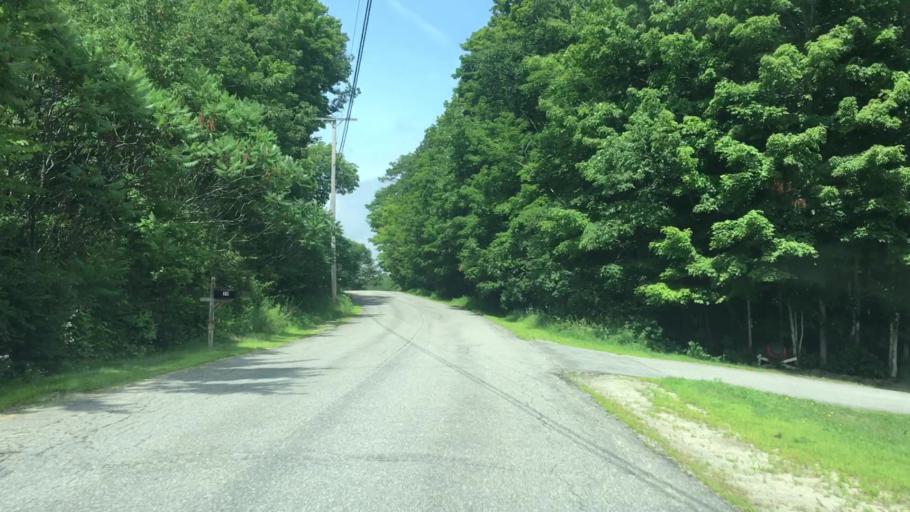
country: US
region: Maine
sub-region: Cumberland County
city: Brunswick
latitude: 43.8884
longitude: -69.9082
